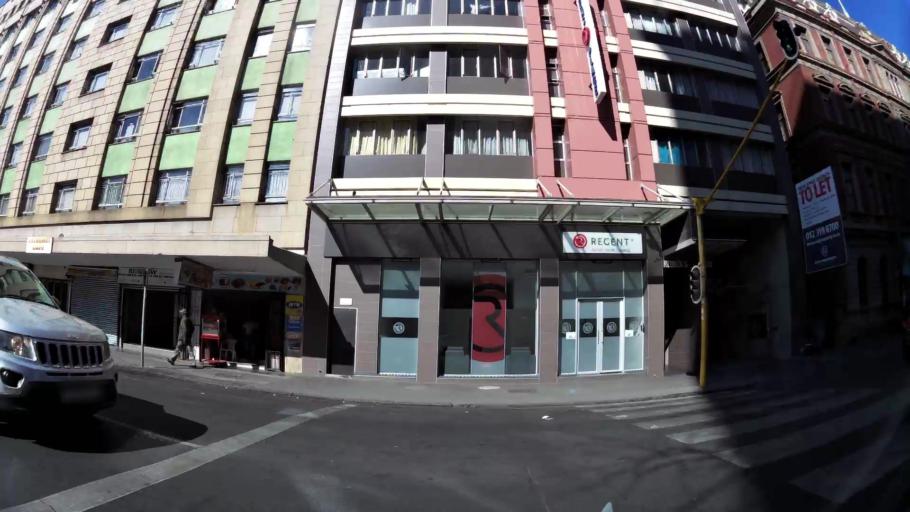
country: ZA
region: Gauteng
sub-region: City of Tshwane Metropolitan Municipality
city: Pretoria
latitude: -25.7481
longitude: 28.1871
